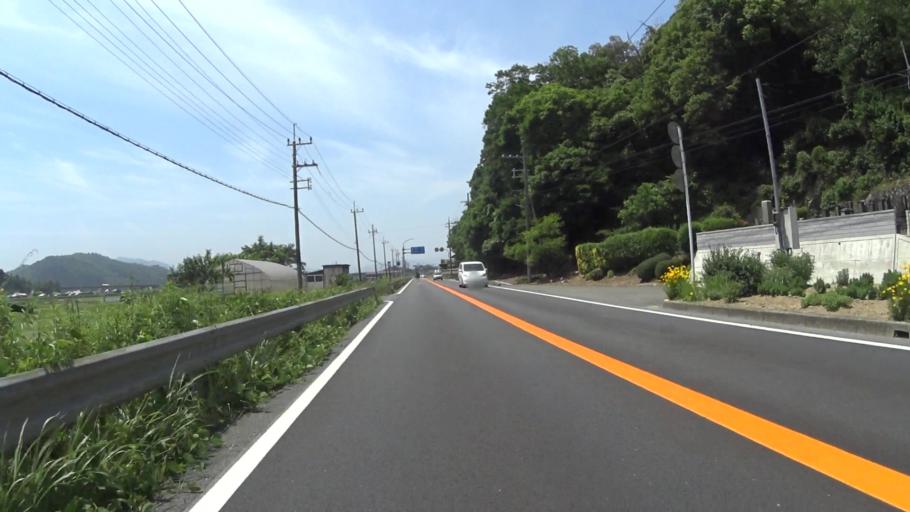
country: JP
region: Kyoto
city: Ayabe
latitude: 35.2610
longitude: 135.1918
